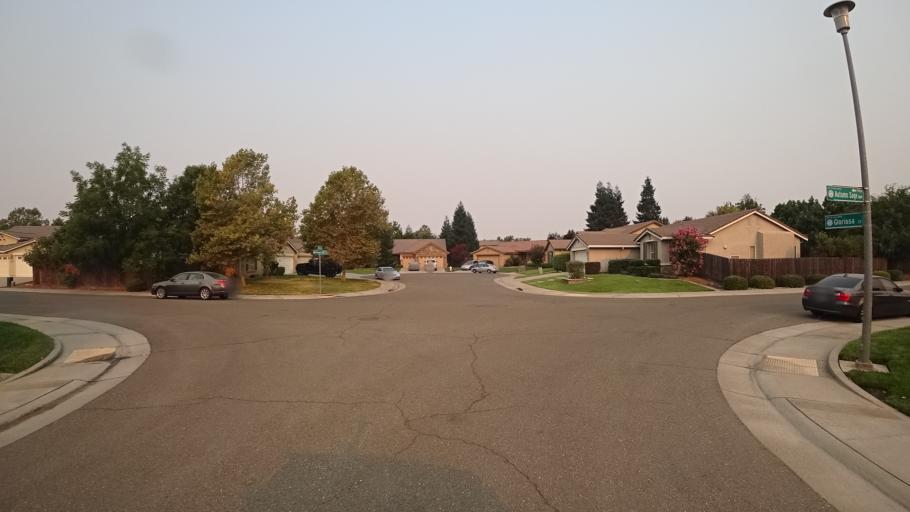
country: US
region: California
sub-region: Sacramento County
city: Laguna
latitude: 38.3957
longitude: -121.4447
